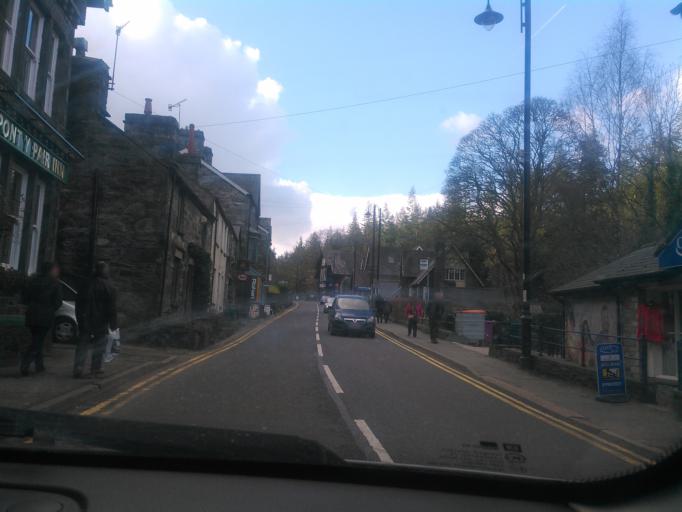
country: GB
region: Wales
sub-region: Conwy
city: Betws-y-Coed
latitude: 53.0937
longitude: -3.8064
